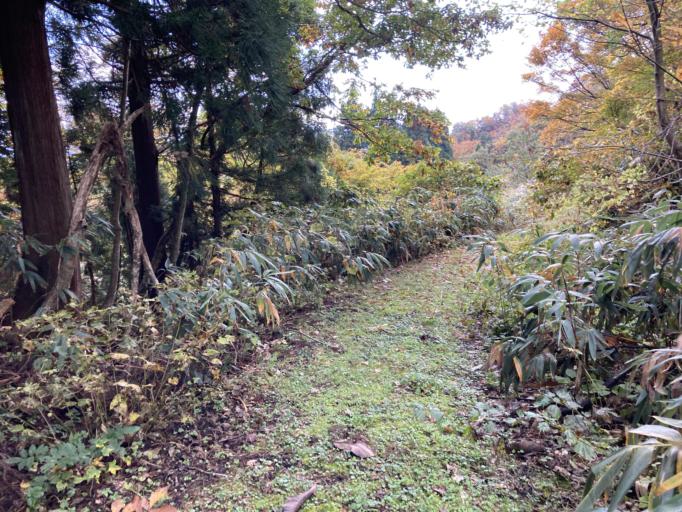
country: JP
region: Niigata
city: Tokamachi
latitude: 37.1571
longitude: 138.6303
